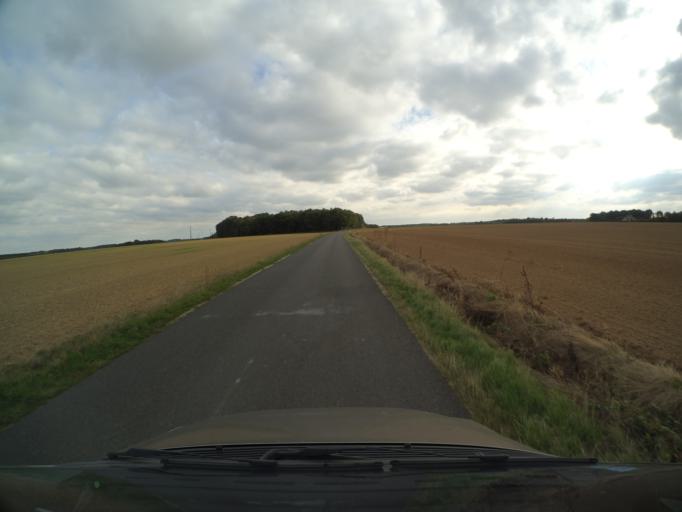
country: FR
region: Centre
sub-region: Departement d'Indre-et-Loire
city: Nazelles-Negron
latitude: 47.4827
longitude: 0.9493
